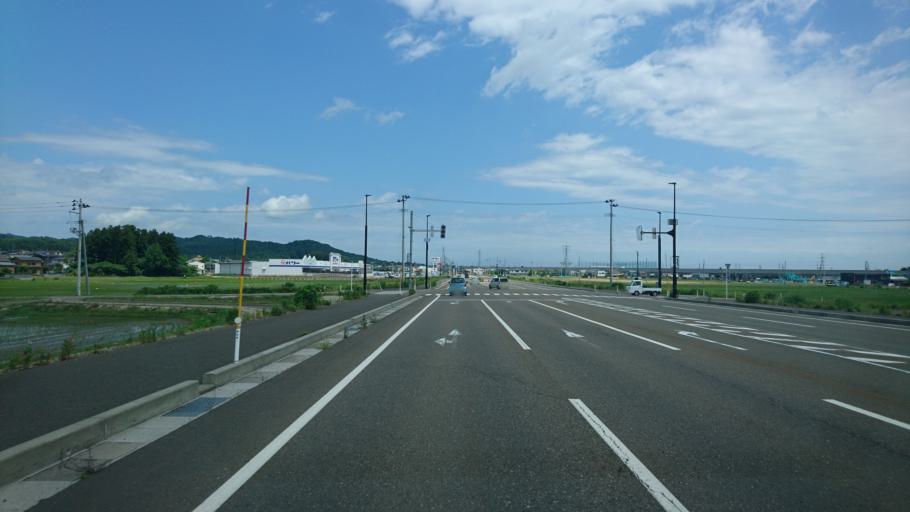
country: JP
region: Niigata
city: Joetsu
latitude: 37.0858
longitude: 138.2337
